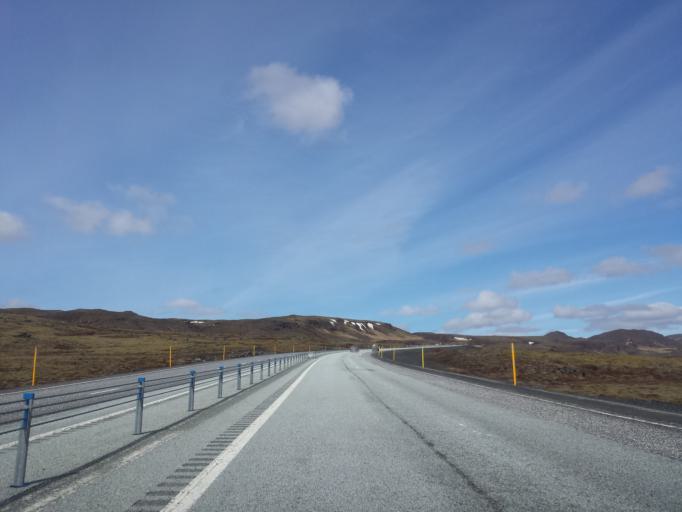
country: IS
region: South
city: Hveragerdi
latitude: 64.0090
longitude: -21.2188
